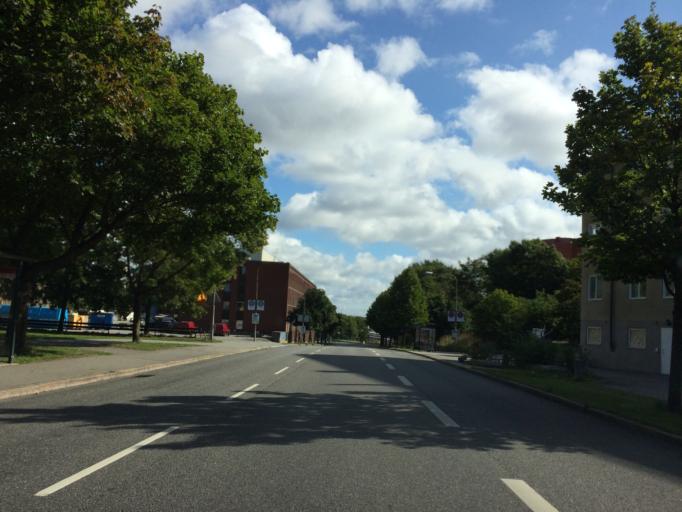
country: SE
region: Stockholm
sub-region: Stockholms Kommun
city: Arsta
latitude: 59.3037
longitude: 18.0071
